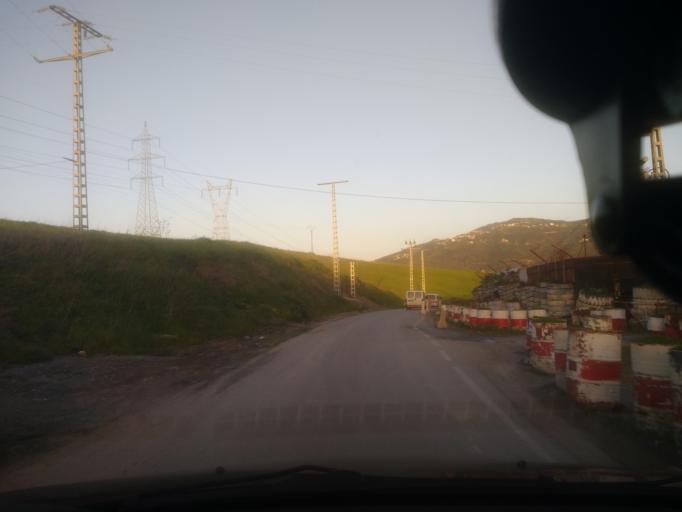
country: DZ
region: Boumerdes
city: Makouda
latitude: 36.7603
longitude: 4.0552
